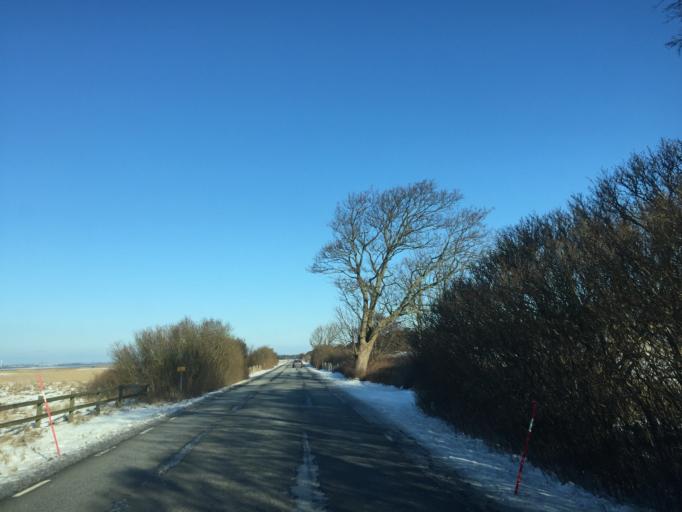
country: SE
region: Skane
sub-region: Kavlinge Kommun
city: Hofterup
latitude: 55.7936
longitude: 12.9380
